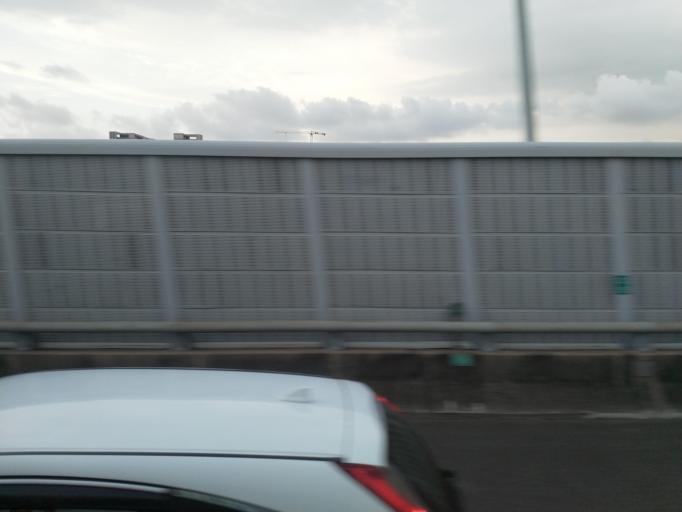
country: TW
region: Taiwan
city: Fengshan
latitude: 22.6786
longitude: 120.3372
